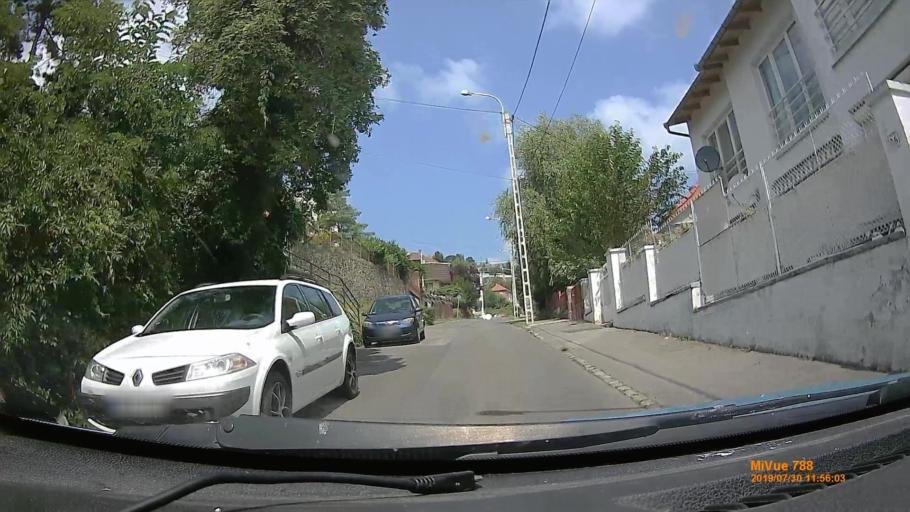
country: HU
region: Baranya
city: Pecs
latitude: 46.0815
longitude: 18.2195
